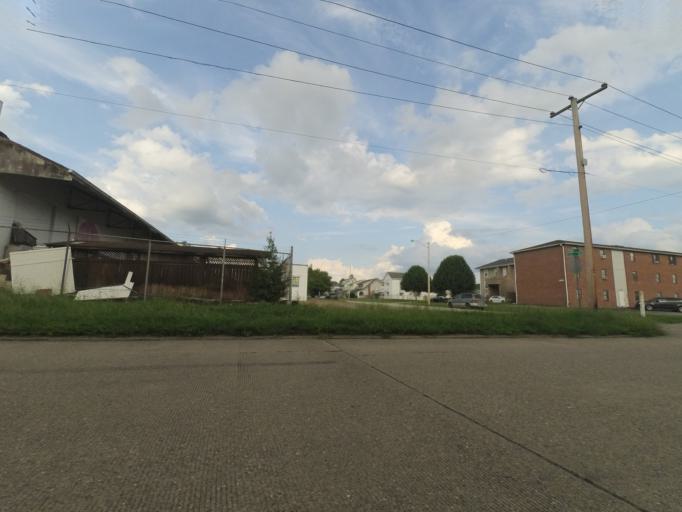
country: US
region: West Virginia
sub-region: Cabell County
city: Huntington
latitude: 38.4282
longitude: -82.4168
